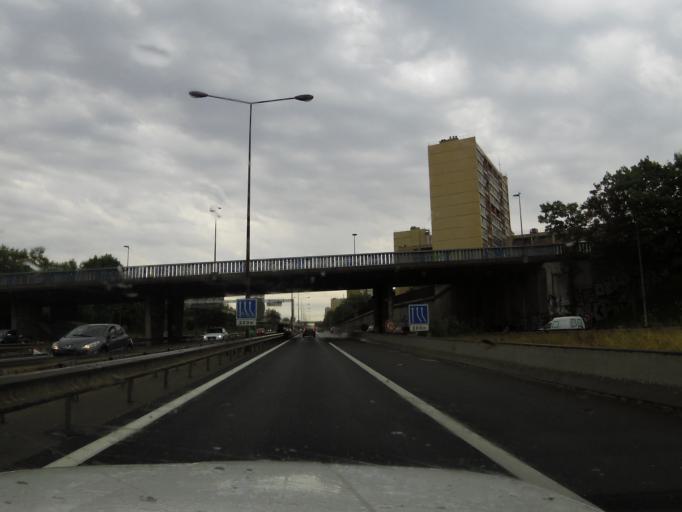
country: FR
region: Rhone-Alpes
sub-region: Departement du Rhone
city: Bron
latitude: 45.7287
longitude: 4.9004
